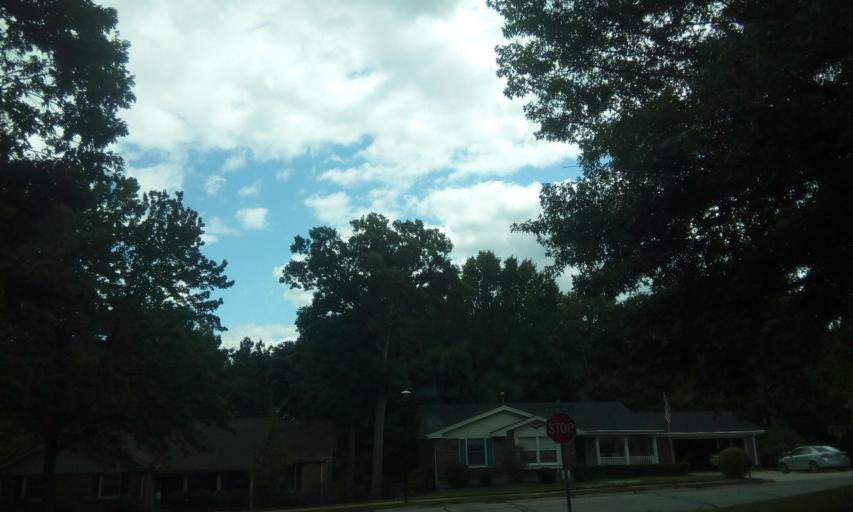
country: US
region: Missouri
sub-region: Saint Louis County
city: Ballwin
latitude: 38.6007
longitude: -90.5440
